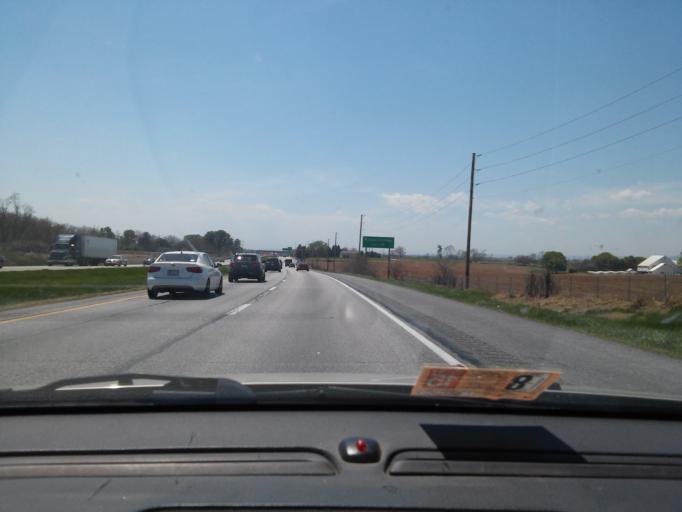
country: US
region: Pennsylvania
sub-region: Franklin County
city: Guilford
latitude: 39.9473
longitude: -77.6144
